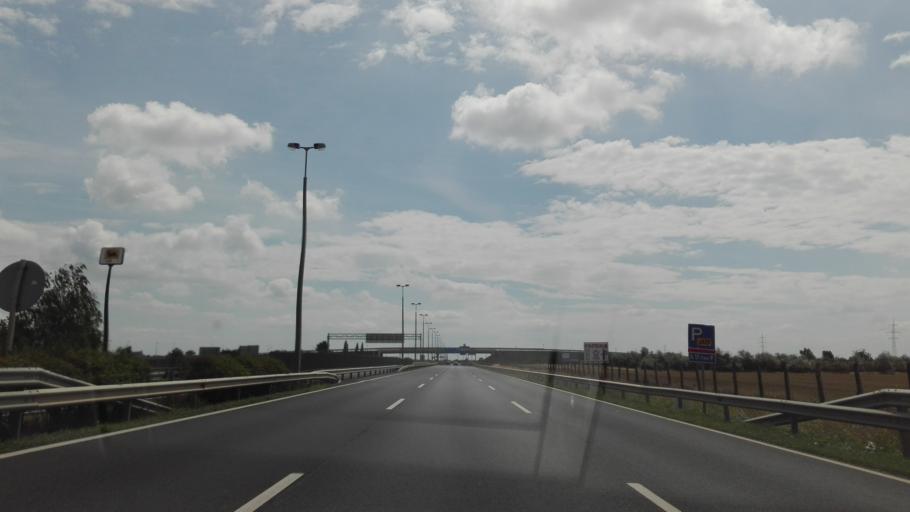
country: AT
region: Burgenland
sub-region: Politischer Bezirk Neusiedl am See
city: Nickelsdorf
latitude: 47.9182
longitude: 17.1206
